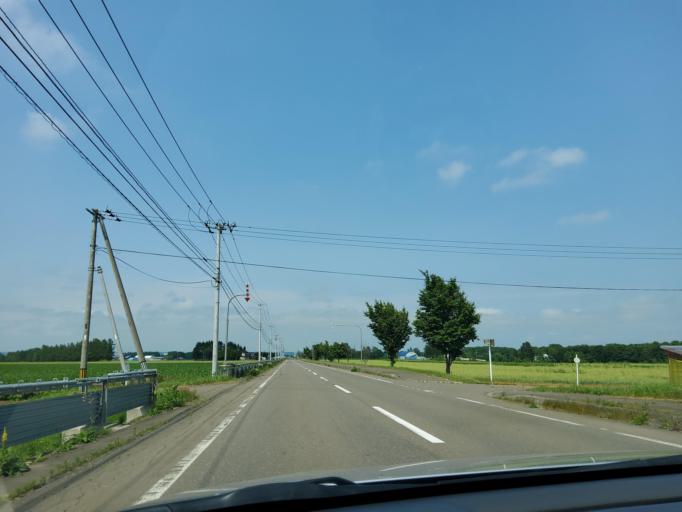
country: JP
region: Hokkaido
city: Obihiro
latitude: 42.8853
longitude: 143.0353
